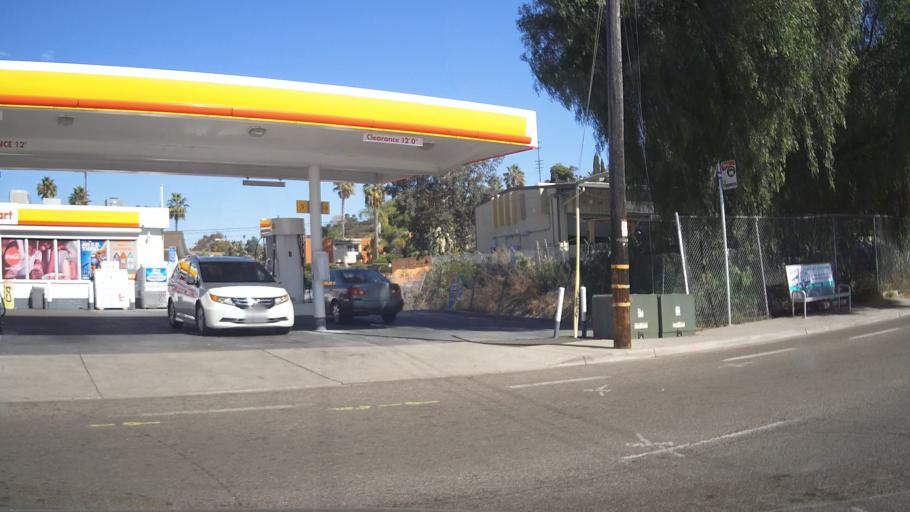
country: US
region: California
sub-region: San Diego County
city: National City
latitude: 32.7286
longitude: -117.0993
